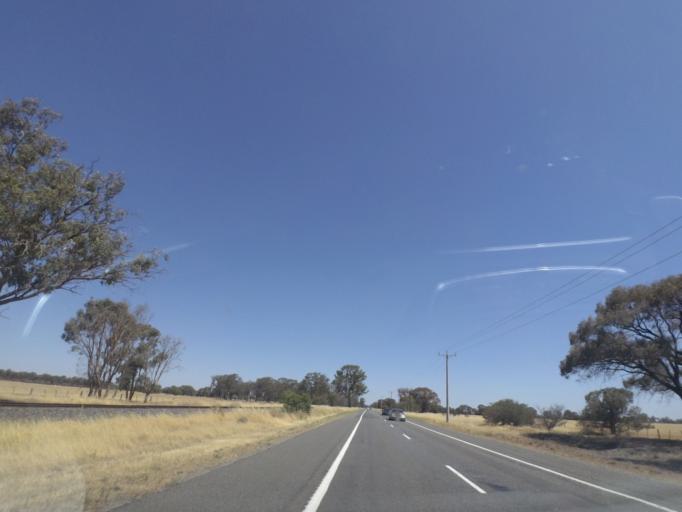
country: AU
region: Victoria
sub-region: Greater Shepparton
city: Shepparton
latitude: -36.2077
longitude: 145.4319
